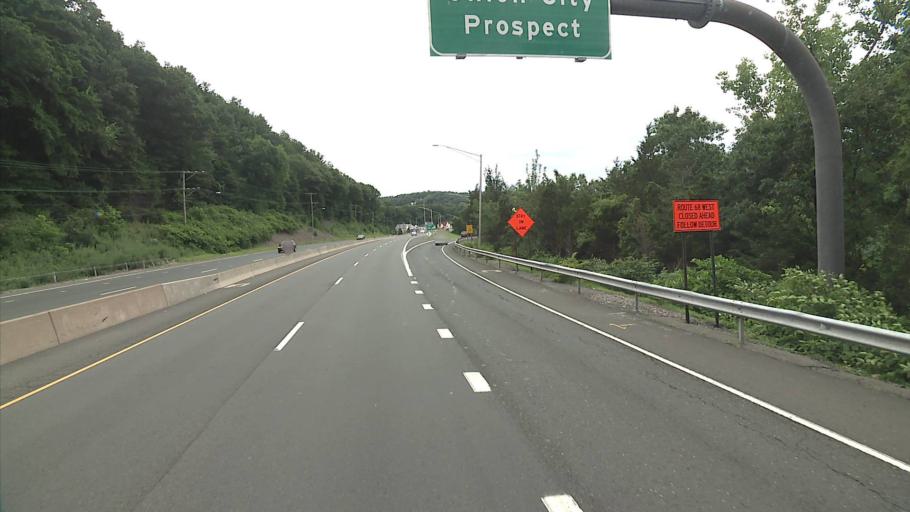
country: US
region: Connecticut
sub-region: New Haven County
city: Naugatuck
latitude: 41.5087
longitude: -73.0462
